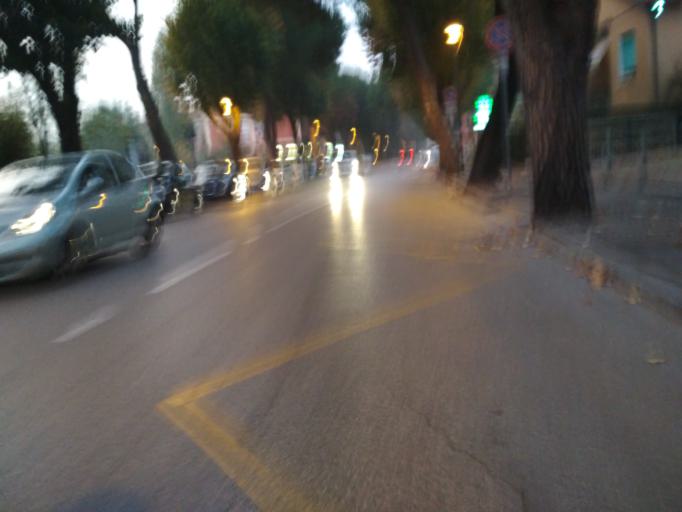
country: IT
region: Emilia-Romagna
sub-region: Provincia di Rimini
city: Rimini
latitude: 44.0700
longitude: 12.5657
